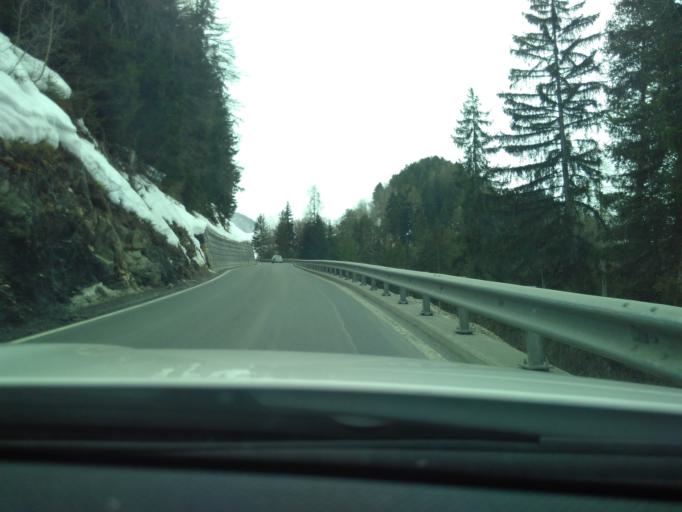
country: CH
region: Grisons
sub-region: Inn District
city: Scuol
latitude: 46.7846
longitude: 10.2772
